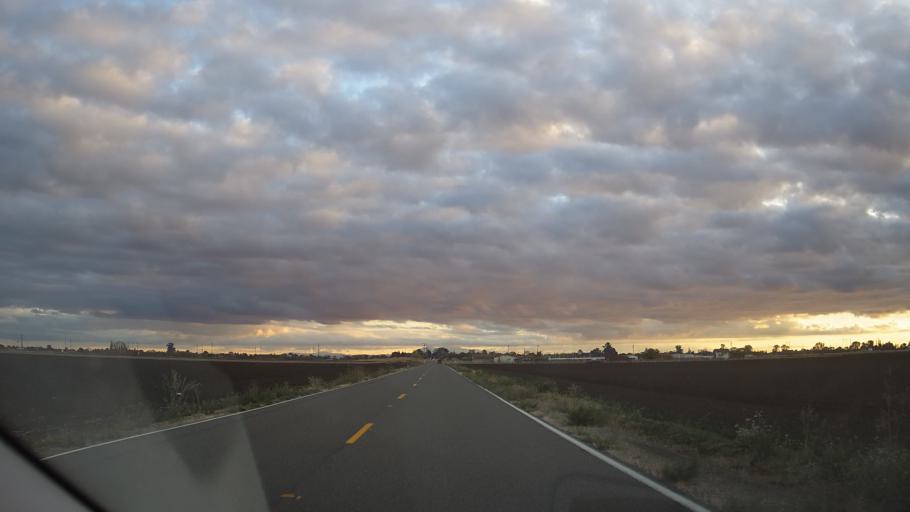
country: US
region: California
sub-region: Solano County
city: Hartley
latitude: 38.3641
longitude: -121.9060
